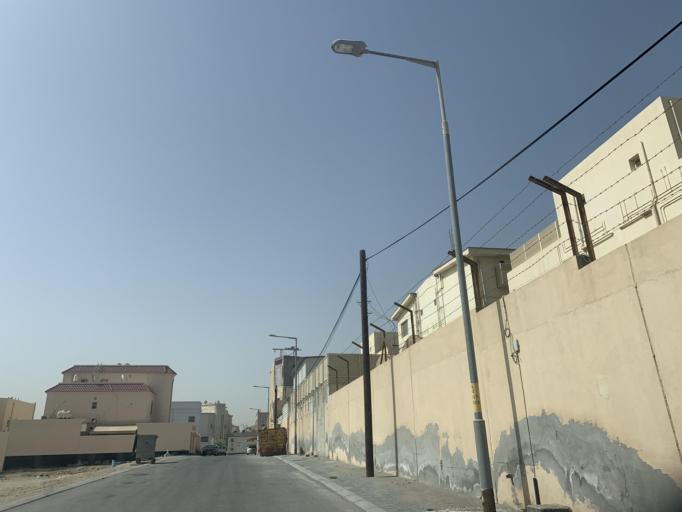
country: BH
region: Northern
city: Madinat `Isa
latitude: 26.1492
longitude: 50.5293
